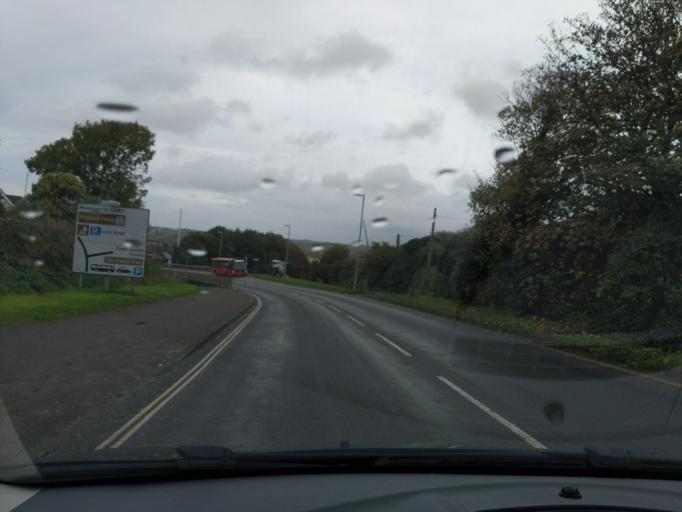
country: GB
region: England
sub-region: Cornwall
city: Padstow
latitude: 50.5373
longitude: -4.9418
